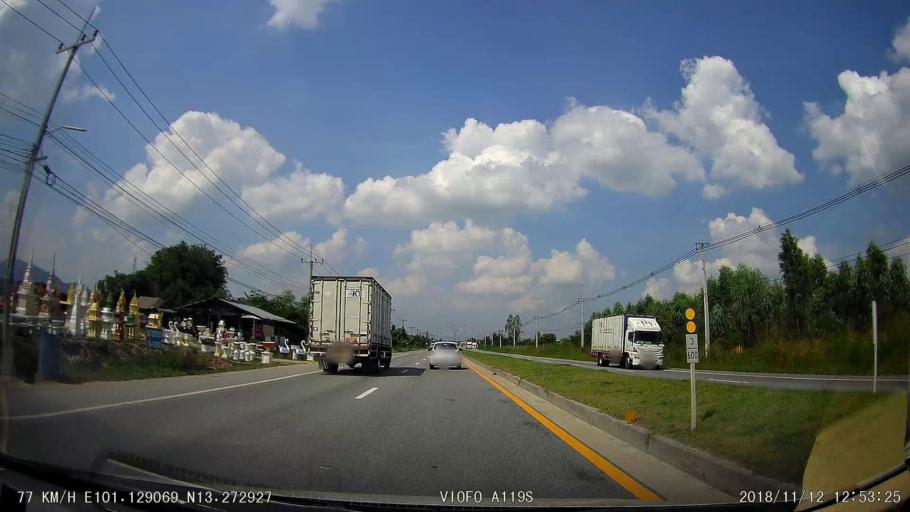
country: TH
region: Chon Buri
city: Ban Bueng
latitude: 13.2732
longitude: 101.1289
